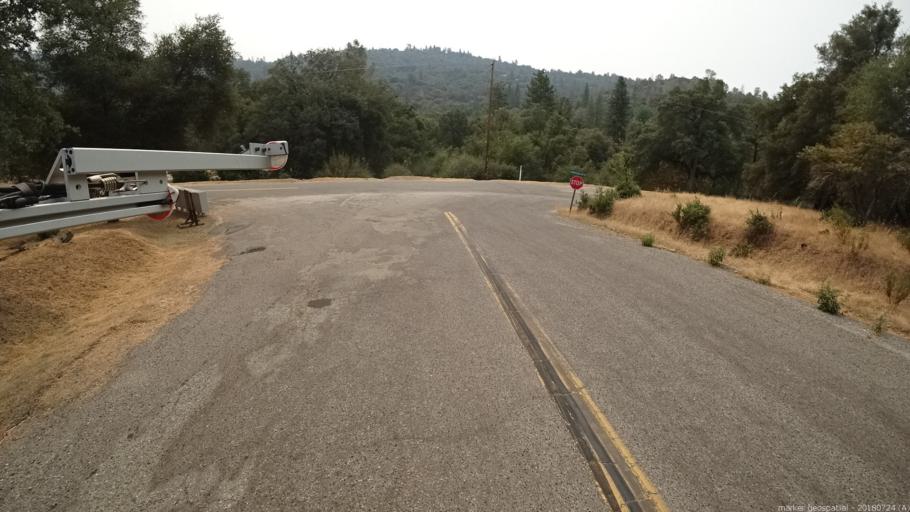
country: US
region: California
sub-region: Madera County
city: Oakhurst
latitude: 37.3332
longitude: -119.6128
